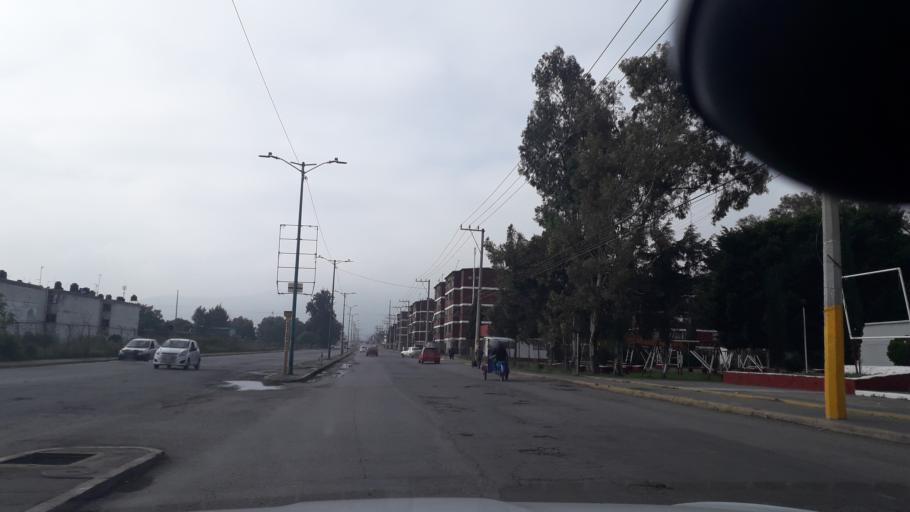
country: MX
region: Mexico
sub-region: Jaltenco
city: Alborada Jaltenco
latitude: 19.6500
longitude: -99.0771
